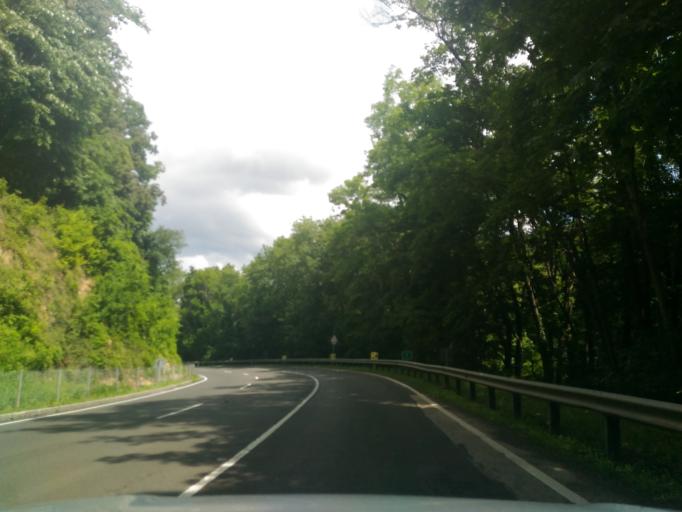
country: HU
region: Baranya
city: Komlo
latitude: 46.1445
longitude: 18.2497
